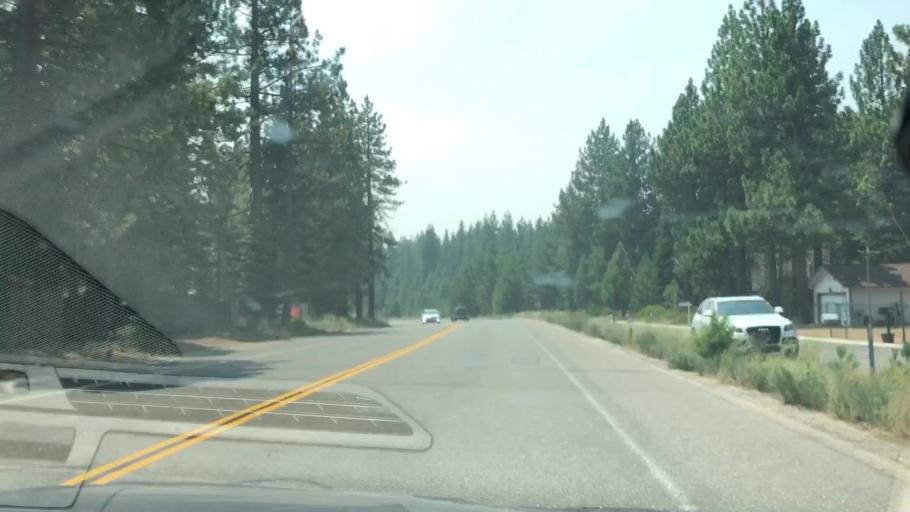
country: US
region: California
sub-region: El Dorado County
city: South Lake Tahoe
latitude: 38.8817
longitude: -119.9883
